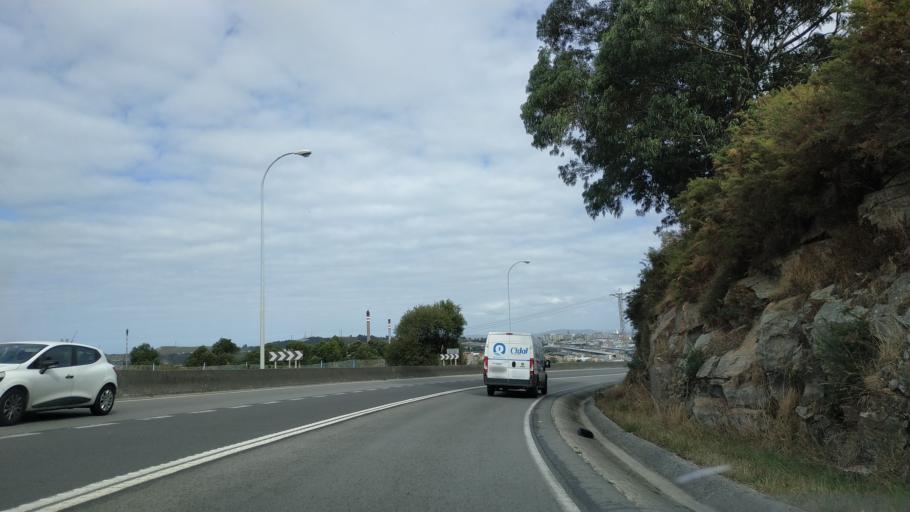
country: ES
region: Galicia
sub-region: Provincia da Coruna
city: Arteixo
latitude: 43.3382
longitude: -8.4539
